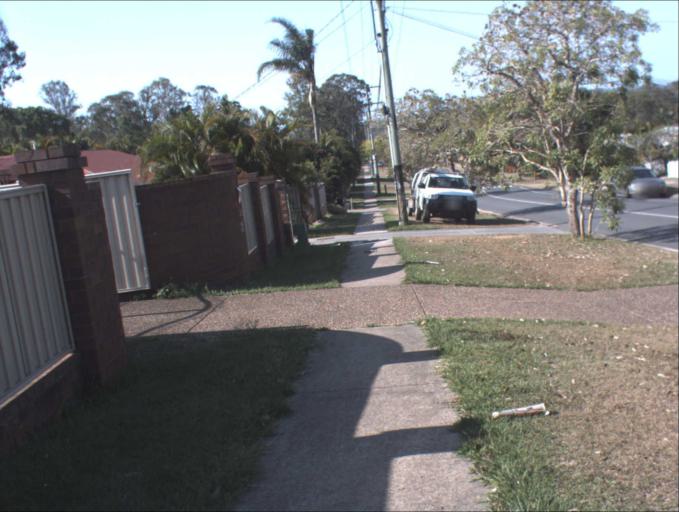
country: AU
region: Queensland
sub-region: Logan
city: Beenleigh
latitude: -27.6935
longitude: 153.1777
